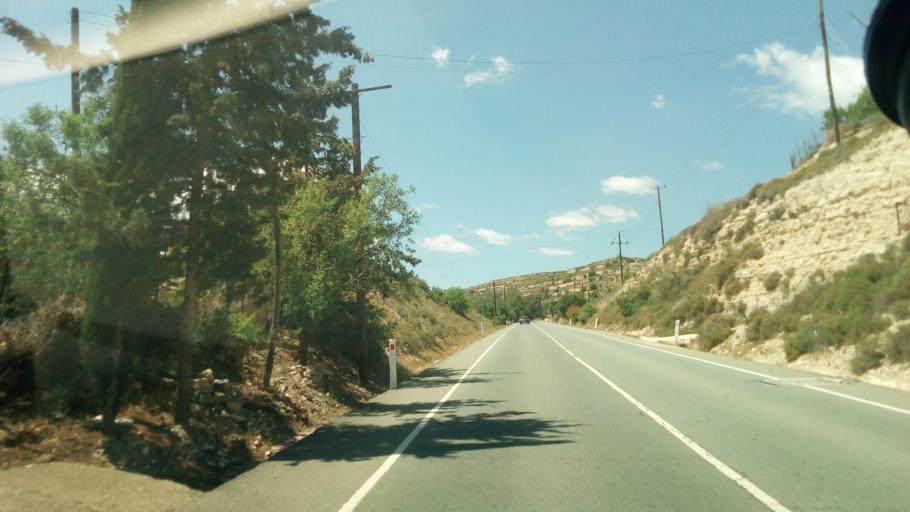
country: CY
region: Limassol
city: Pachna
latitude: 34.7944
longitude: 32.8195
